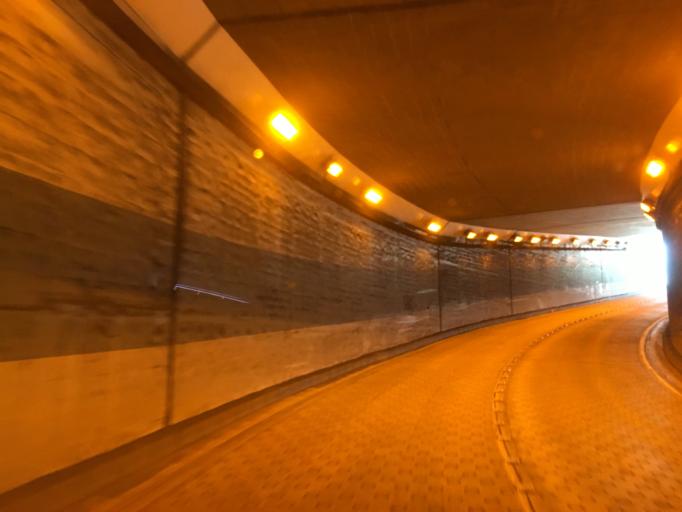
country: JP
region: Tokyo
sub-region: Machida-shi
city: Machida
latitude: 35.5318
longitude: 139.4979
